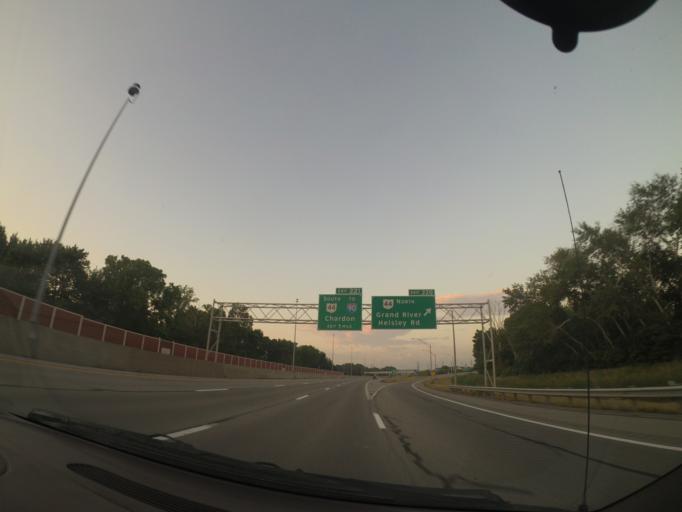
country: US
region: Ohio
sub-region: Lake County
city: Fairport Harbor
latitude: 41.7162
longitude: -81.3036
